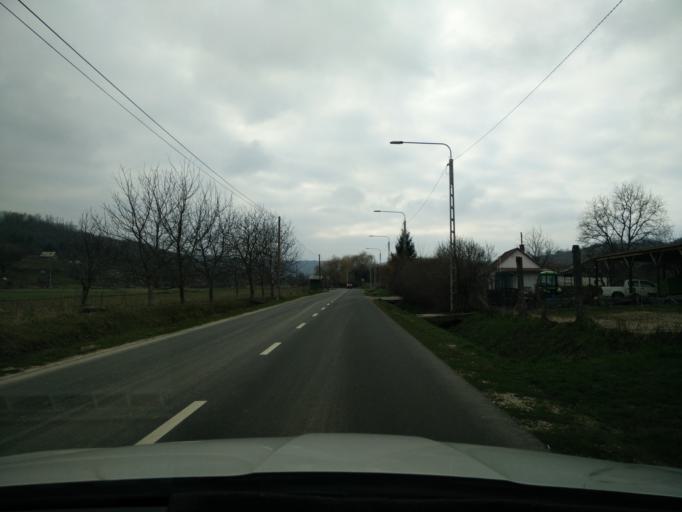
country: HU
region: Tolna
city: Szekszard
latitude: 46.3312
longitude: 18.6832
